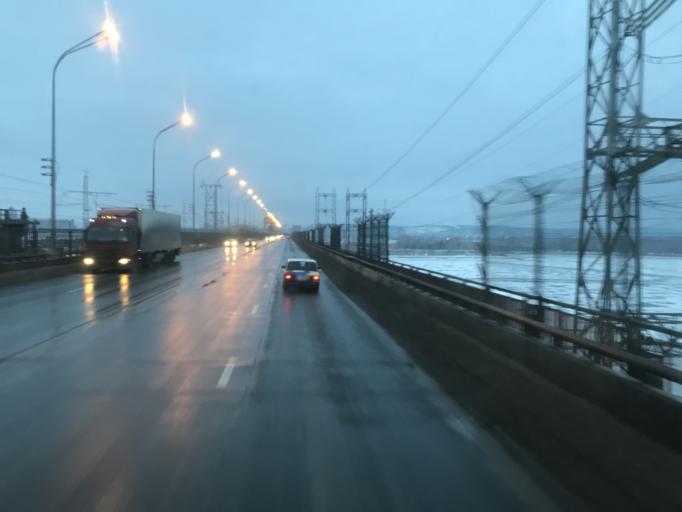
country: RU
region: Samara
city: Zhigulevsk
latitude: 53.4543
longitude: 49.4937
